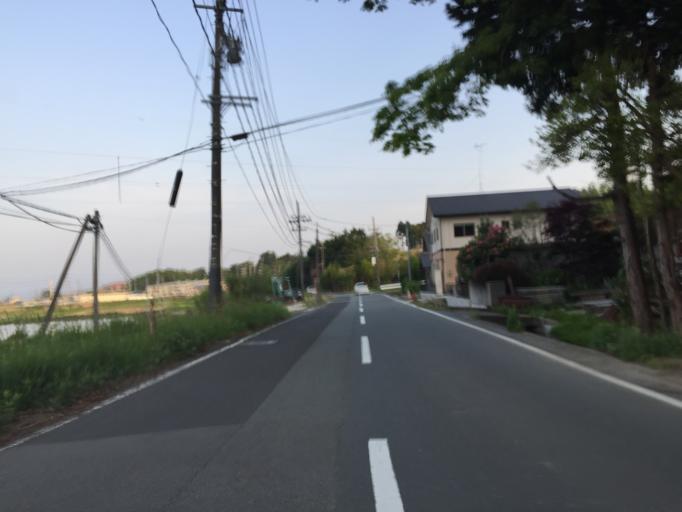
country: JP
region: Fukushima
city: Namie
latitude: 37.2698
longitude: 140.9910
